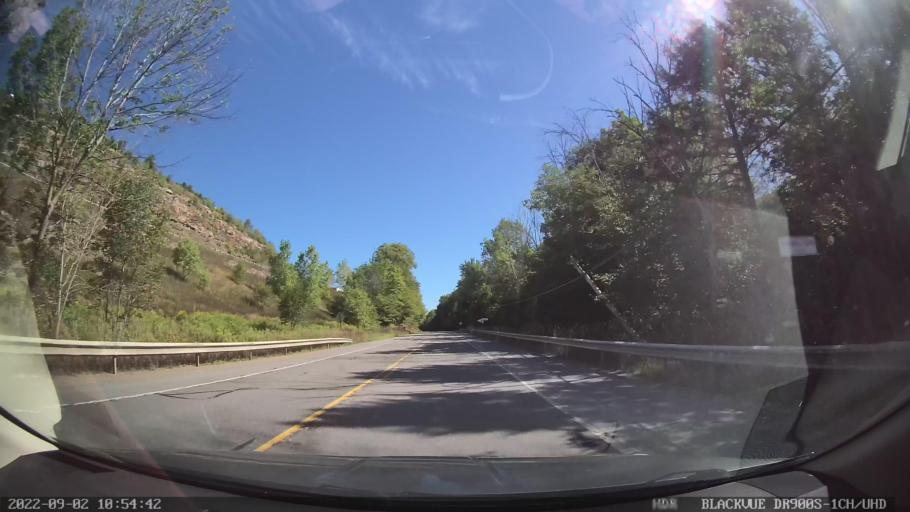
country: US
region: Pennsylvania
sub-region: Tioga County
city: Blossburg
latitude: 41.6610
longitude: -77.0872
